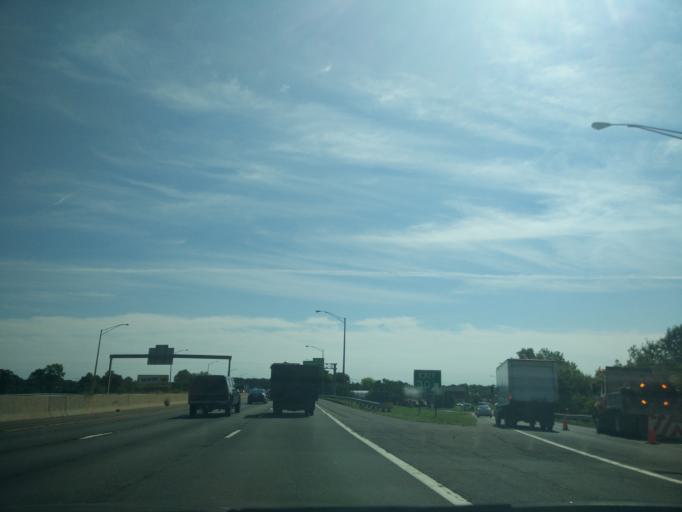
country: US
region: Connecticut
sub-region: Fairfield County
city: Stratford
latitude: 41.1747
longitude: -73.1618
